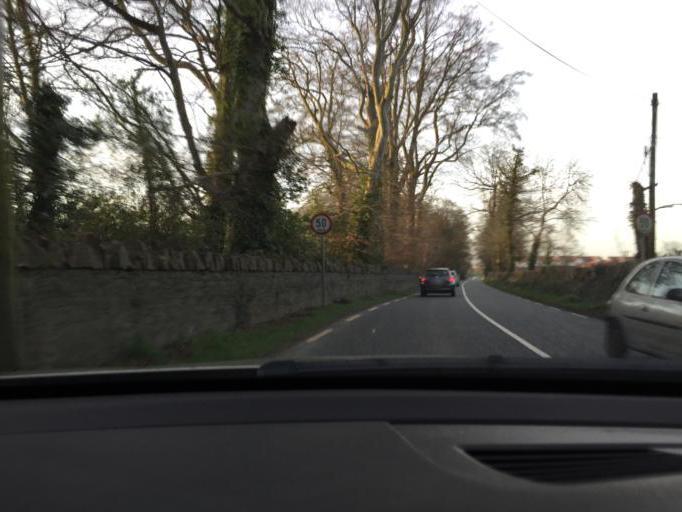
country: IE
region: Leinster
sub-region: An Mhi
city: Dunboyne
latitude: 53.4043
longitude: -6.4457
